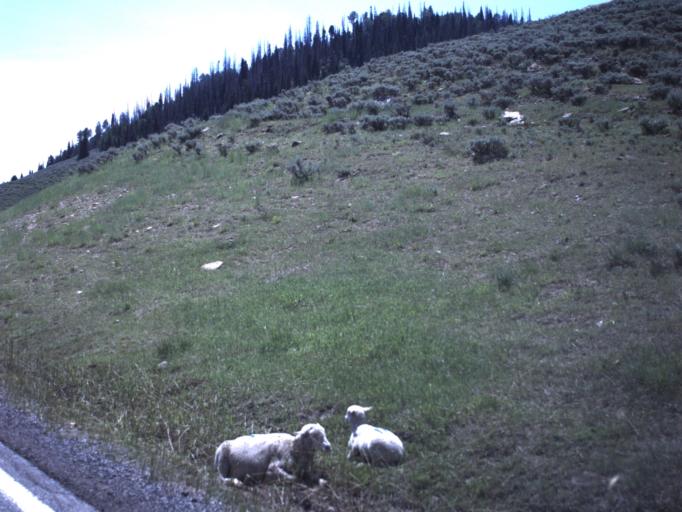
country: US
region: Utah
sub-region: Sanpete County
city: Fairview
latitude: 39.6646
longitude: -111.2442
